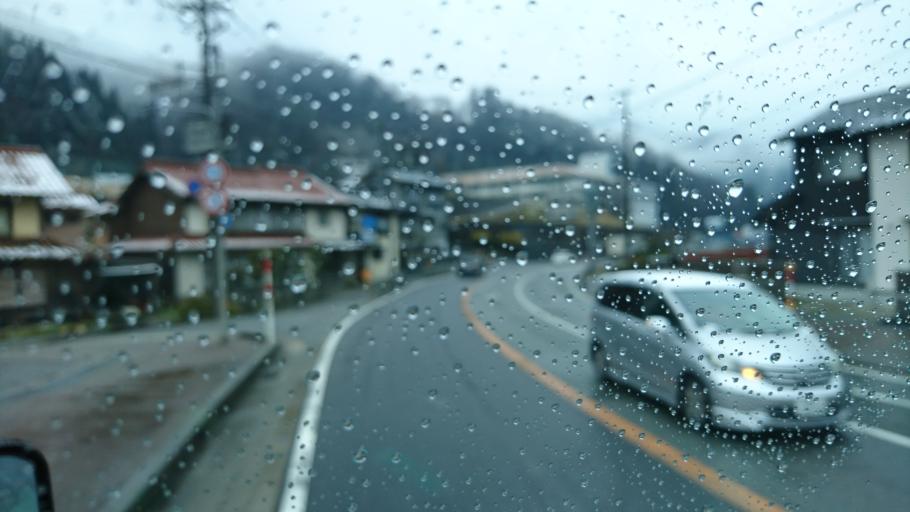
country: JP
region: Tottori
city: Tottori
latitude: 35.5608
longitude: 134.4841
